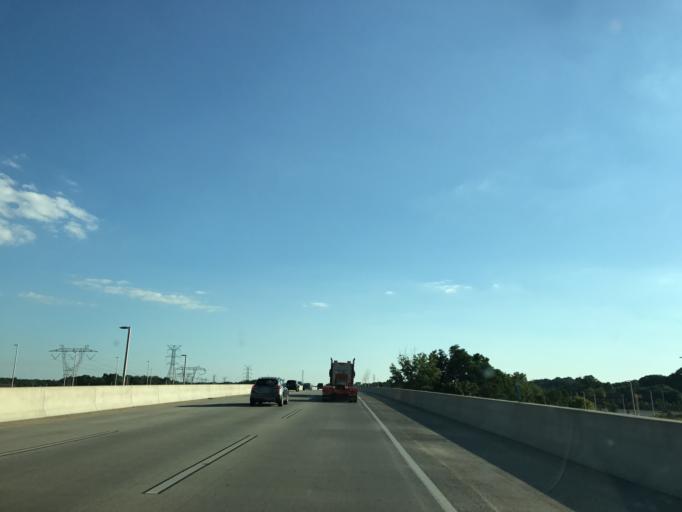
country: US
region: New Jersey
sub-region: Burlington County
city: Bordentown
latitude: 40.1293
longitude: -74.6949
